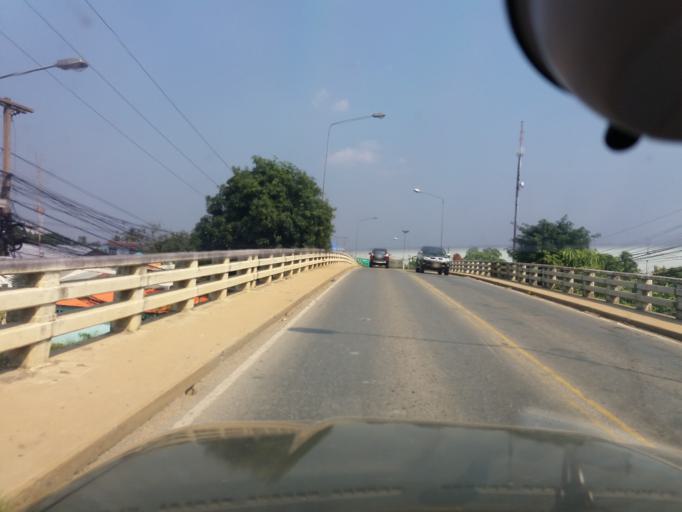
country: TH
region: Sing Buri
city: Bang Racham
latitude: 14.8884
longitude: 100.3173
